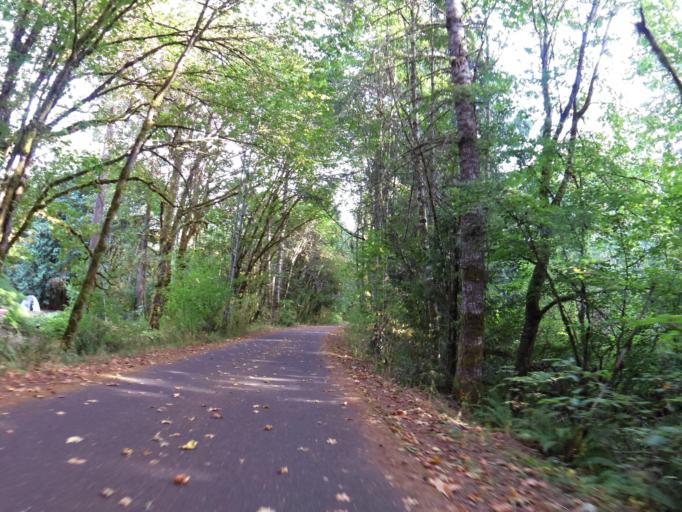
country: US
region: Washington
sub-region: Thurston County
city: Lacey
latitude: 46.9778
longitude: -122.8134
